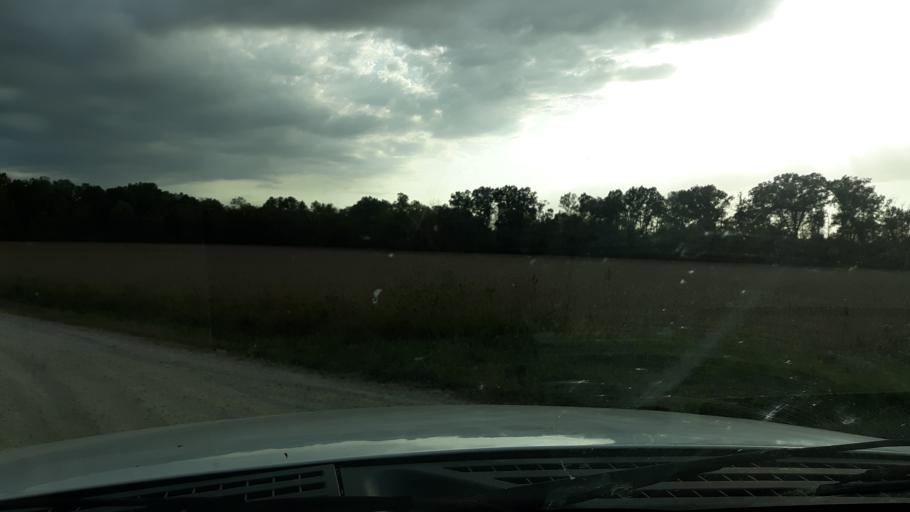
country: US
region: Illinois
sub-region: Saline County
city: Eldorado
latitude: 37.8342
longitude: -88.5025
